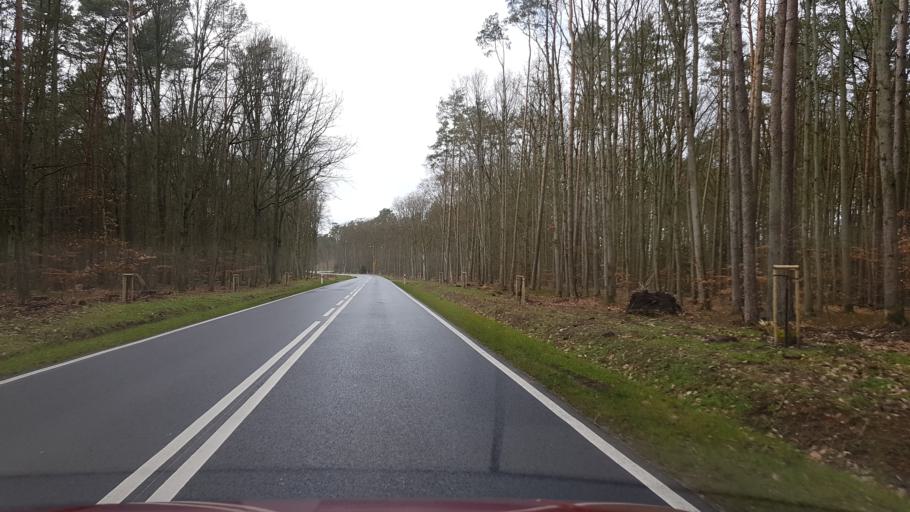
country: PL
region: West Pomeranian Voivodeship
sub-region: Powiat policki
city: Nowe Warpno
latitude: 53.6710
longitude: 14.4078
